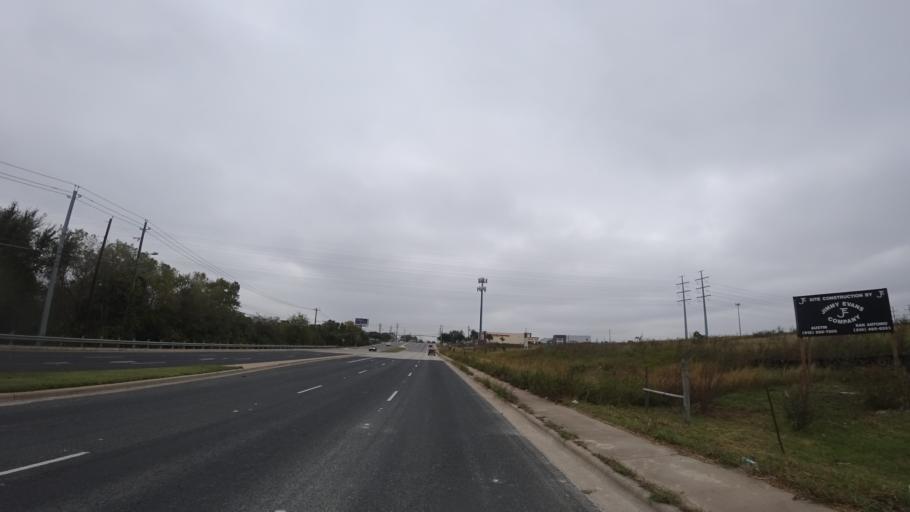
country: US
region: Texas
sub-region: Travis County
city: Pflugerville
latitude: 30.3840
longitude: -97.6498
